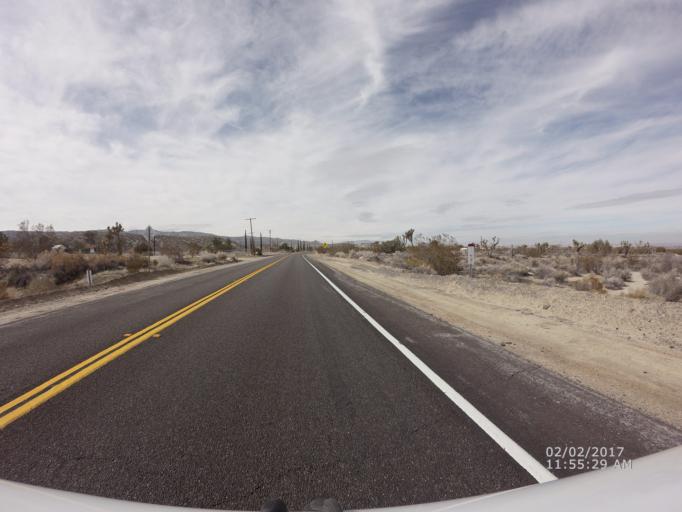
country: US
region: California
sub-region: Los Angeles County
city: Littlerock
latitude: 34.4921
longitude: -117.9418
